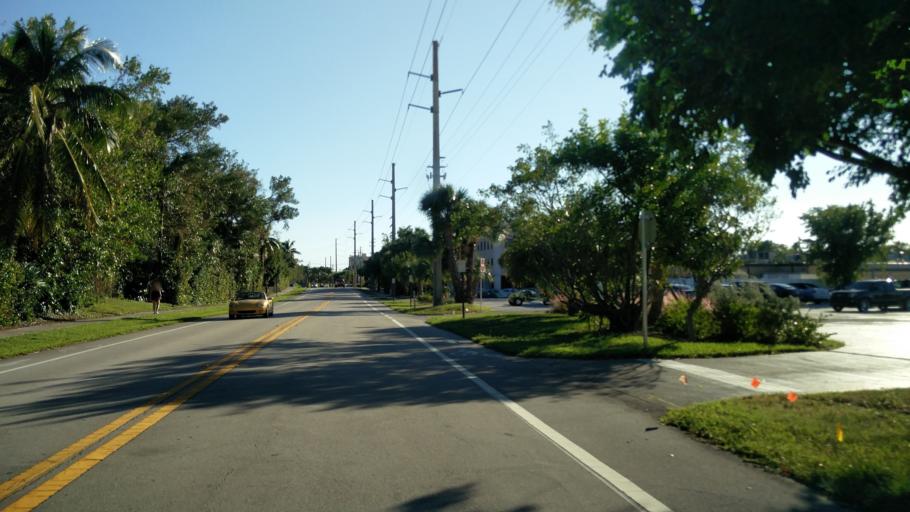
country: US
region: Florida
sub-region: Palm Beach County
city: Juno Beach
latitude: 26.8657
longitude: -80.0538
